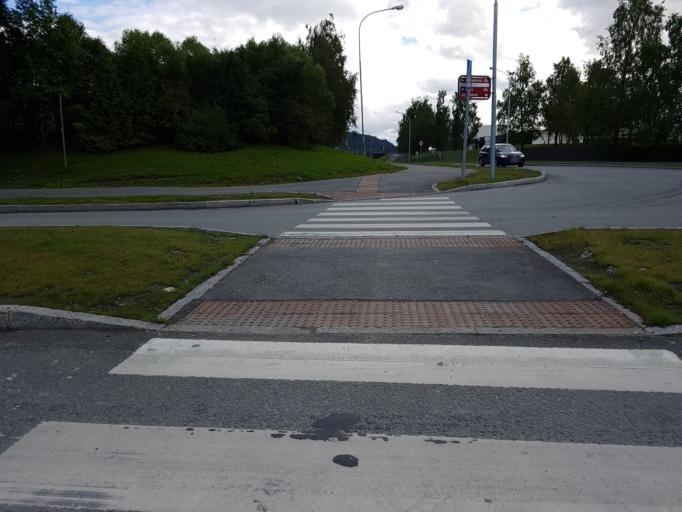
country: NO
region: Sor-Trondelag
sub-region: Trondheim
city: Trondheim
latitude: 63.3906
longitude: 10.4281
